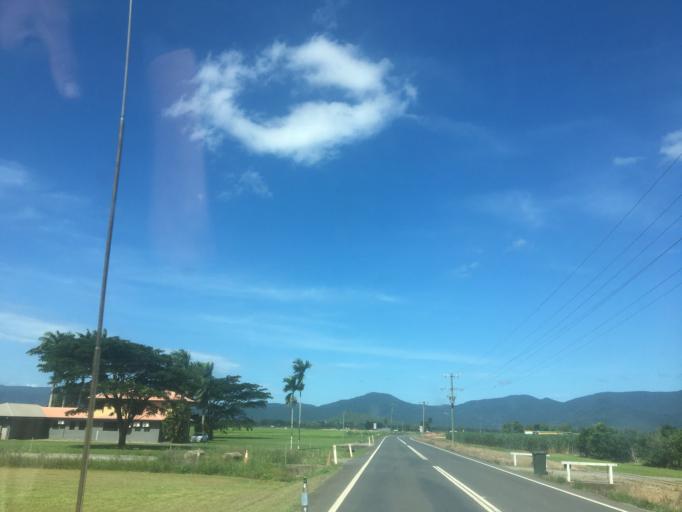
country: AU
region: Queensland
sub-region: Cairns
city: Woree
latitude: -17.0611
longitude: 145.7635
